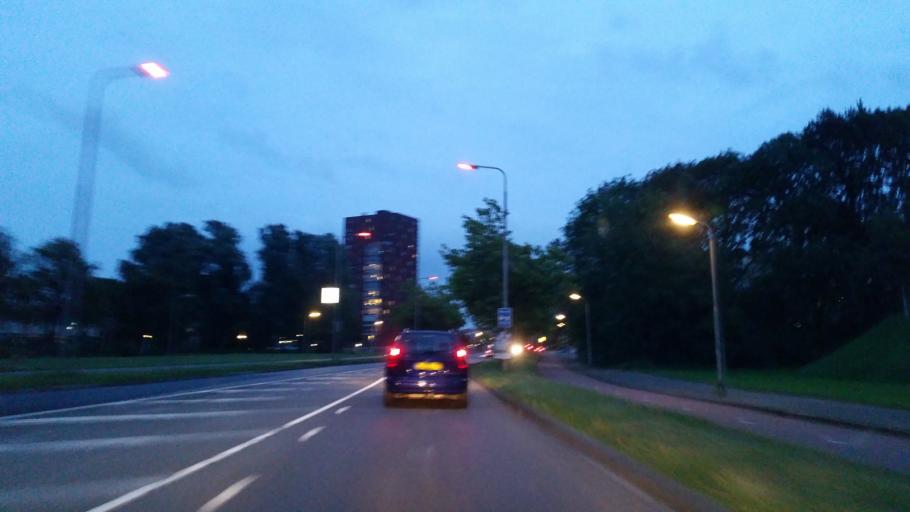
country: NL
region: Friesland
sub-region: Gemeente Leeuwarden
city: Bilgaard
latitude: 53.2131
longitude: 5.8001
